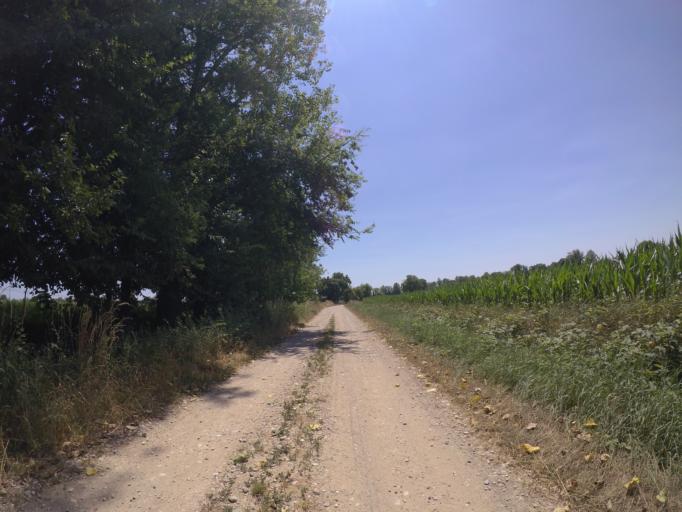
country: IT
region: Friuli Venezia Giulia
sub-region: Provincia di Udine
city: Talmassons
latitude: 45.9270
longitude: 13.0920
